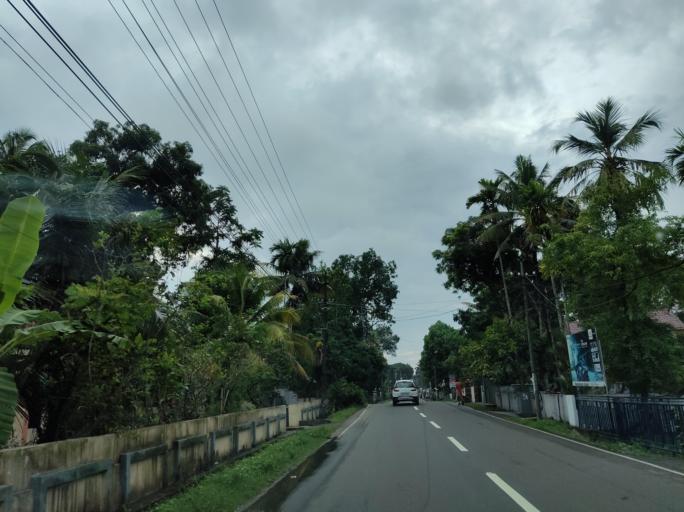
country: IN
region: Kerala
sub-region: Alappuzha
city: Mavelikara
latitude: 9.2516
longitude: 76.5198
